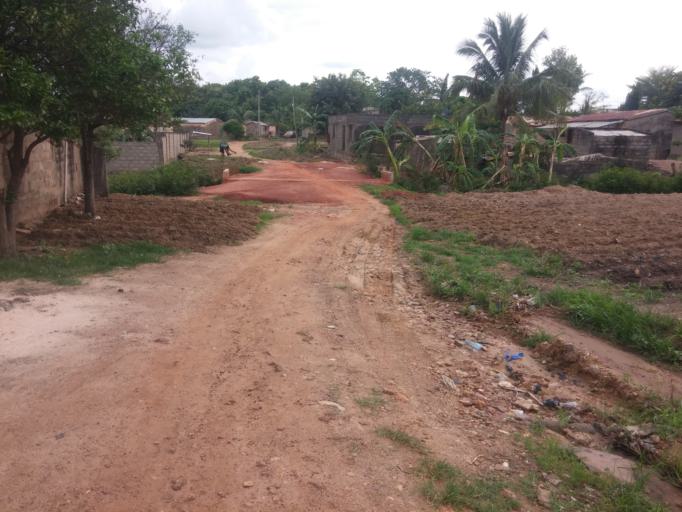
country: TG
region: Kara
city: Kara
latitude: 9.5459
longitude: 1.2042
